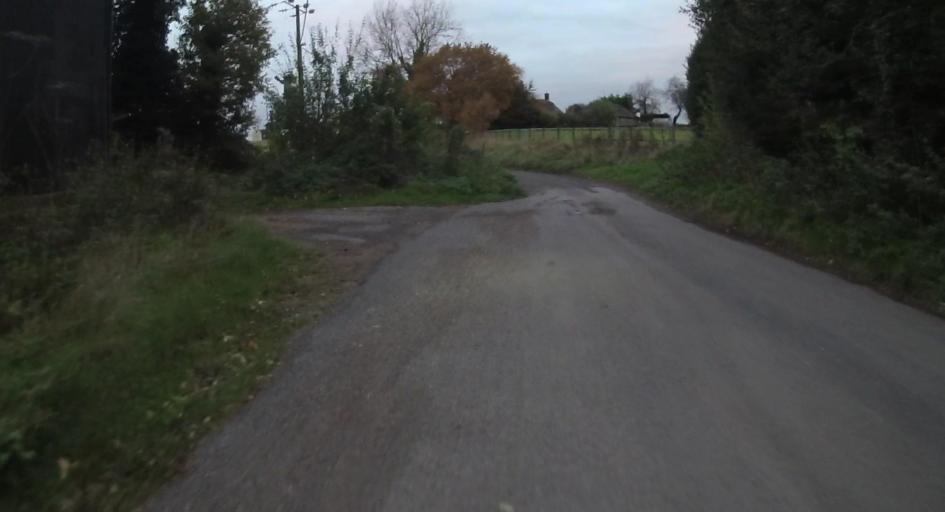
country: GB
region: England
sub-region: Hampshire
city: Kingsley
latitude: 51.1634
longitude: -0.8819
